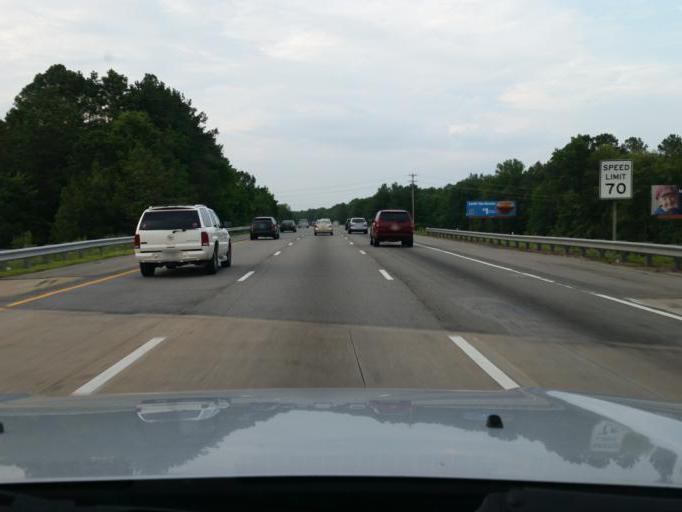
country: US
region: Virginia
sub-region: Hanover County
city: Ashland
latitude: 37.8567
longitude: -77.4539
